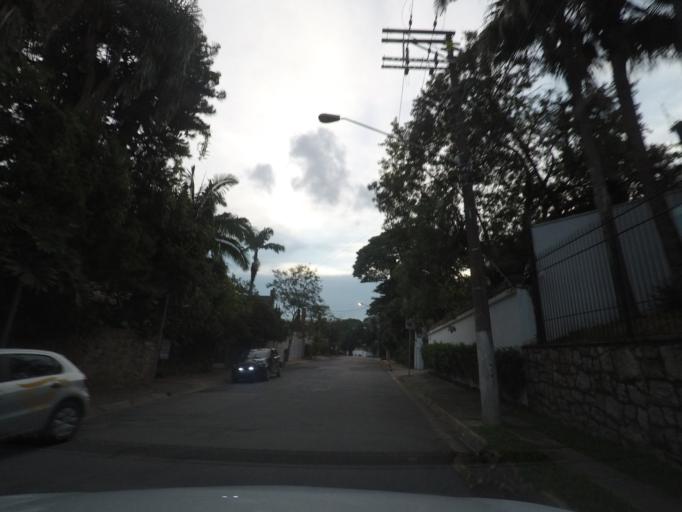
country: BR
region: Sao Paulo
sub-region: Taboao Da Serra
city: Taboao da Serra
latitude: -23.6154
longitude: -46.7082
